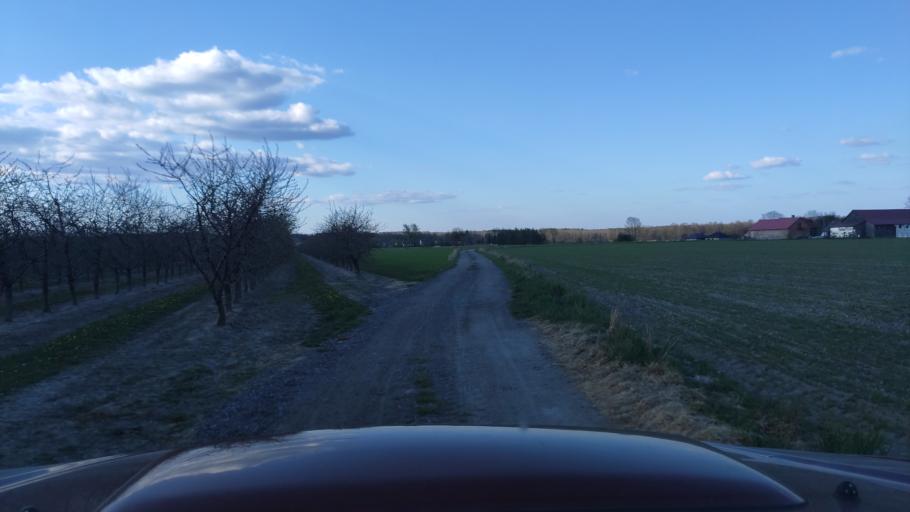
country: PL
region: Masovian Voivodeship
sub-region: Powiat zwolenski
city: Zwolen
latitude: 51.3780
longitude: 21.5750
